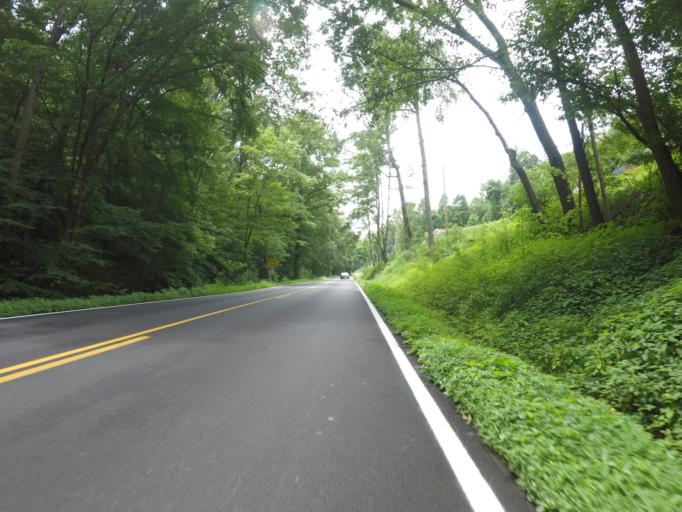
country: US
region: Kentucky
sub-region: Boyd County
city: Catlettsburg
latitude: 38.4346
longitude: -82.6277
